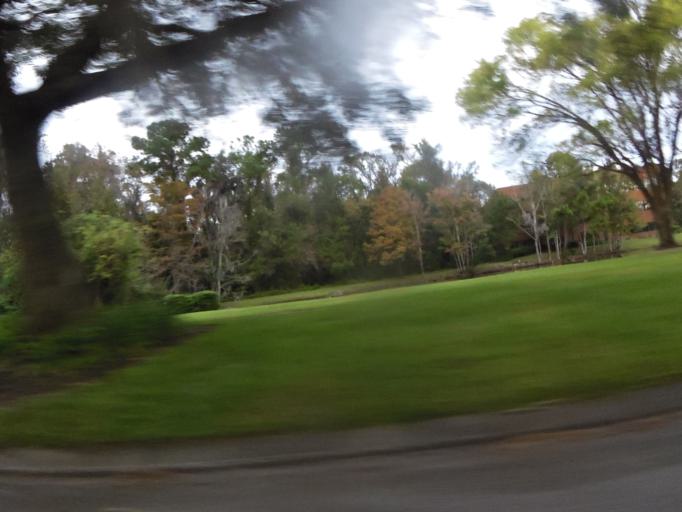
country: US
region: Florida
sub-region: Duval County
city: Jacksonville
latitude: 30.2424
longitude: -81.5829
